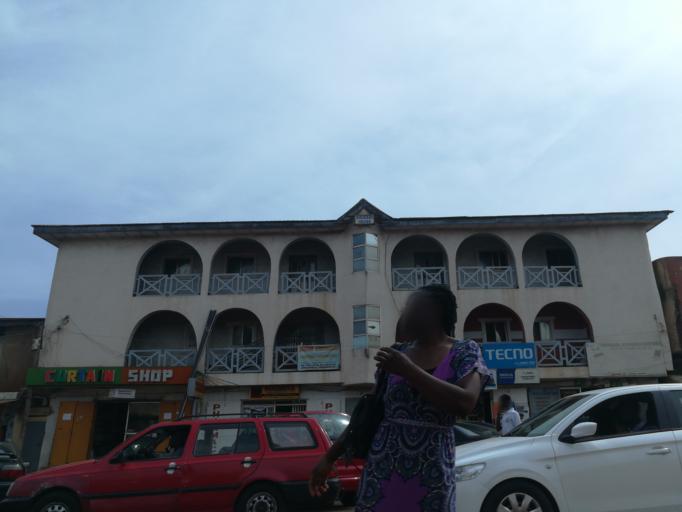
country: NG
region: Plateau
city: Jos
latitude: 9.9147
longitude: 8.8896
